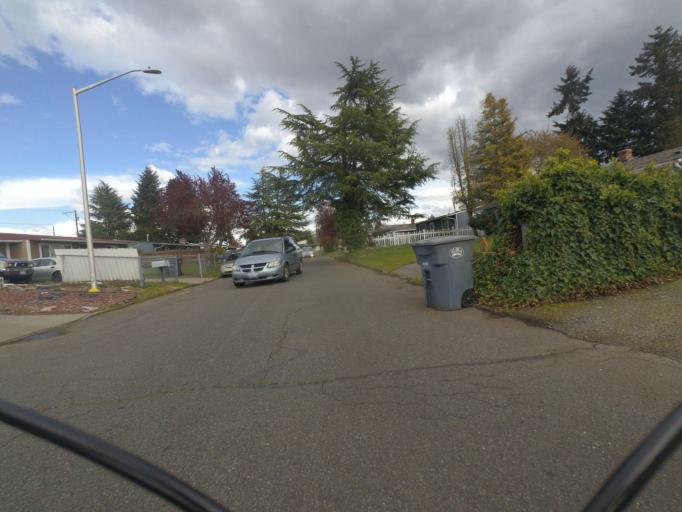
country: US
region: Washington
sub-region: Pierce County
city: Lakewood
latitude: 47.1661
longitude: -122.4972
